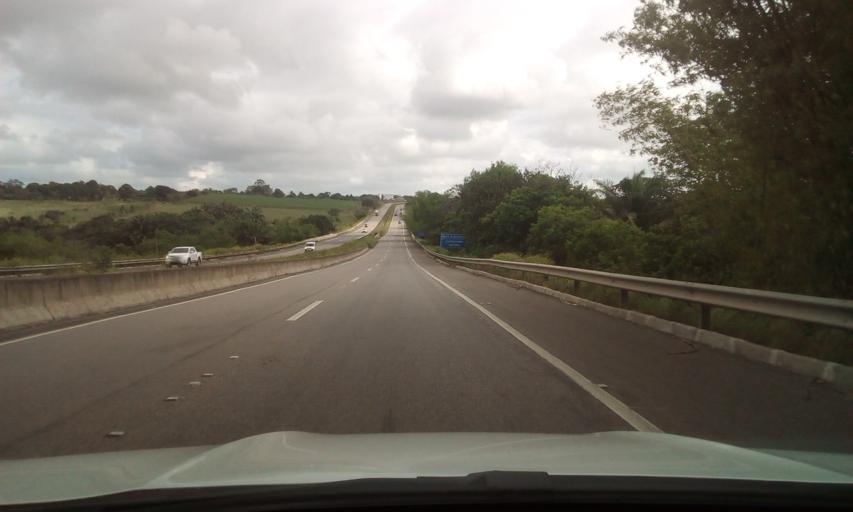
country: BR
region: Pernambuco
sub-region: Itapissuma
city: Itapissuma
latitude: -7.6886
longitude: -34.9224
